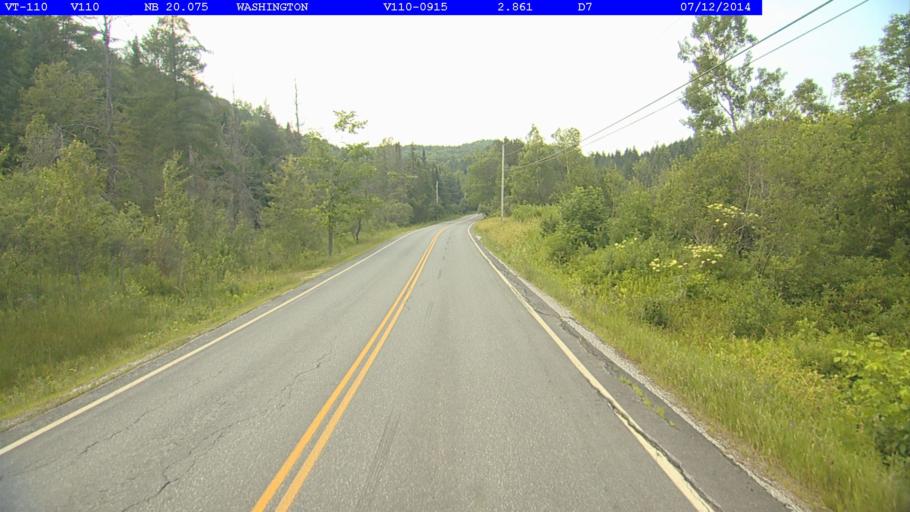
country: US
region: Vermont
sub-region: Orange County
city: Chelsea
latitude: 44.0761
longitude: -72.4617
